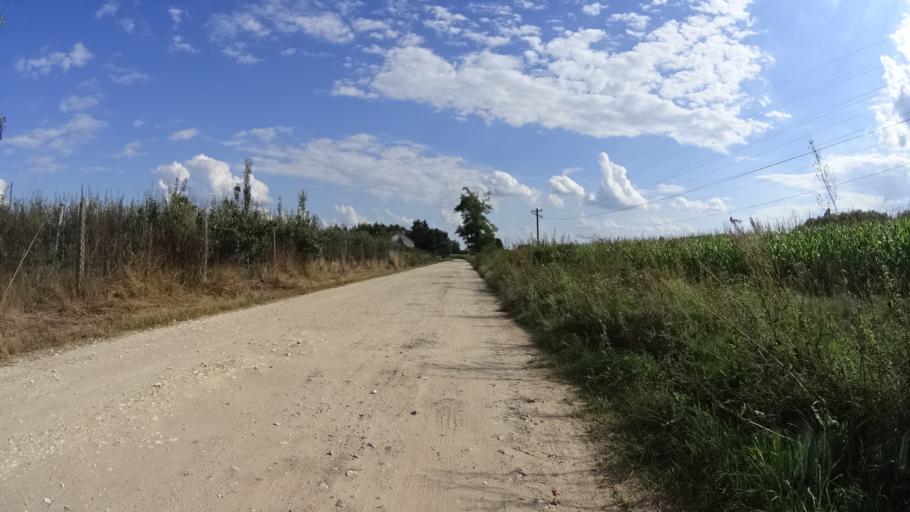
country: PL
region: Masovian Voivodeship
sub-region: Powiat grojecki
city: Mogielnica
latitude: 51.6800
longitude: 20.7640
